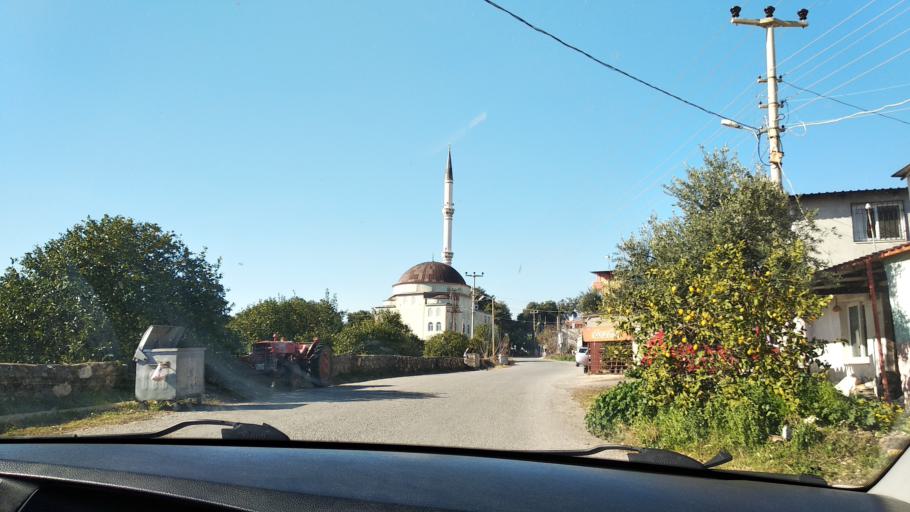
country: TR
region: Mersin
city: Tomuk
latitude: 36.6675
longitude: 34.3581
